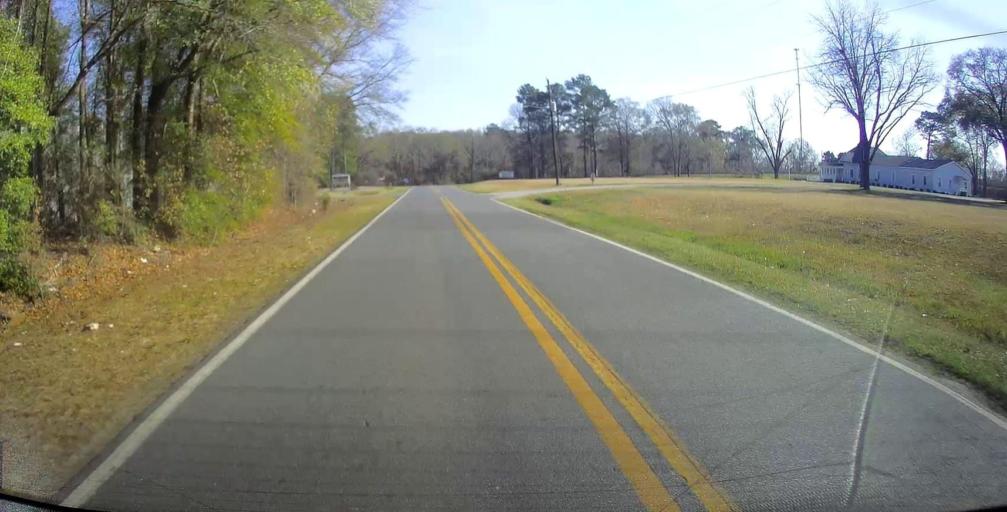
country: US
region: Georgia
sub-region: Macon County
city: Oglethorpe
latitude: 32.2975
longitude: -84.0561
